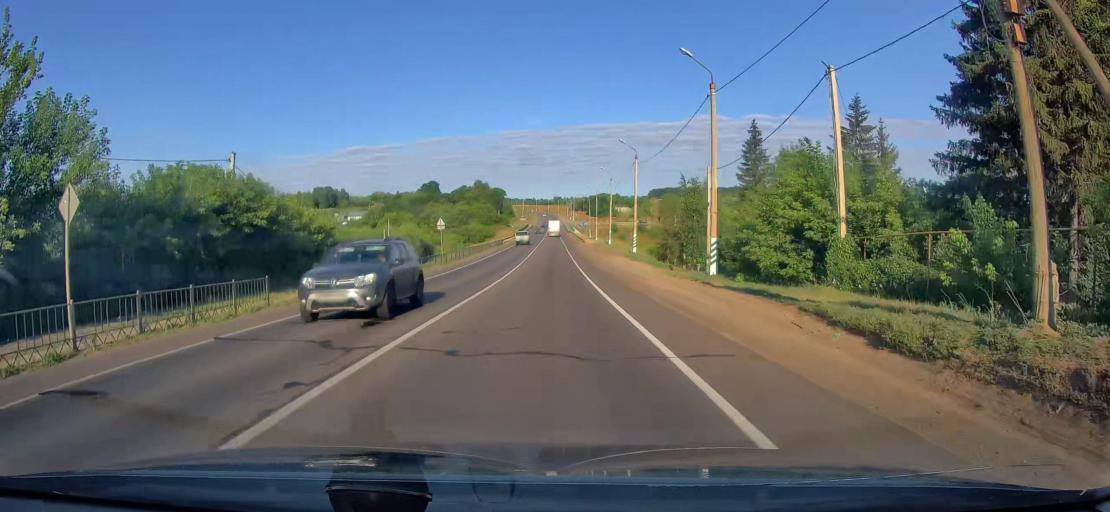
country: RU
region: Tula
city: Chern'
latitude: 53.4543
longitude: 36.9058
